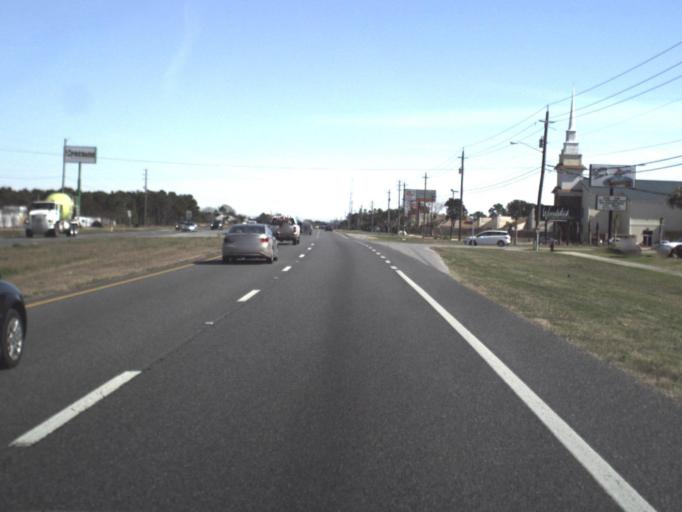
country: US
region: Florida
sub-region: Bay County
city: Laguna Beach
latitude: 30.2353
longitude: -85.9027
